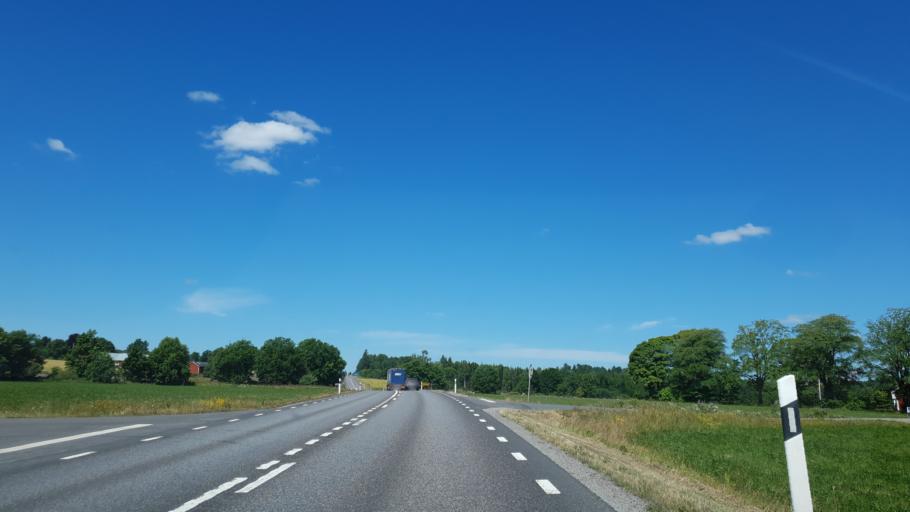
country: SE
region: Joenkoeping
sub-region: Varnamo Kommun
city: Rydaholm
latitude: 56.9959
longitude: 14.2889
